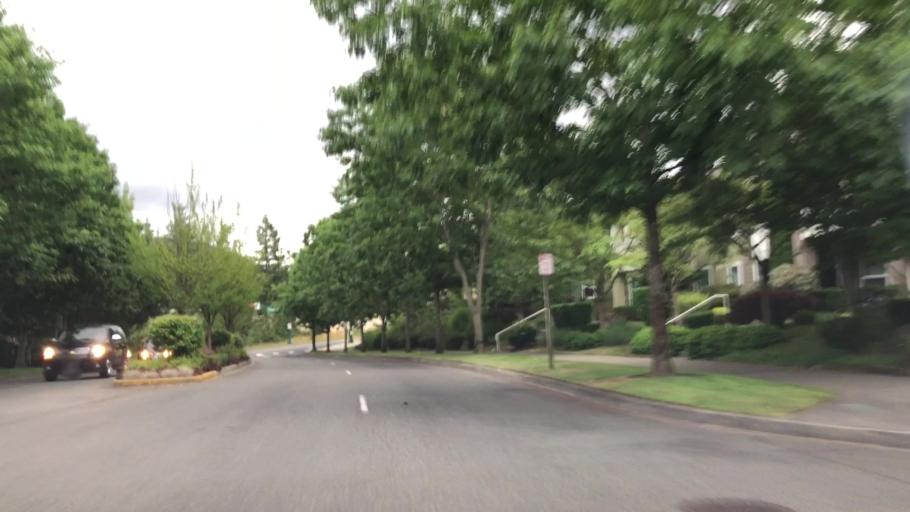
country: US
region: Washington
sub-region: King County
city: Fall City
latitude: 47.5312
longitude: -121.8684
